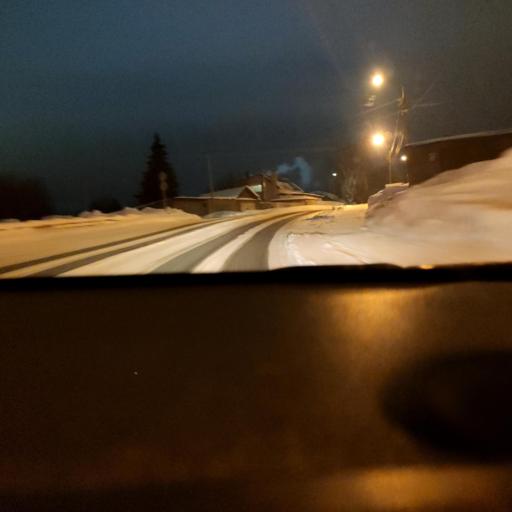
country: RU
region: Tatarstan
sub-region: Chistopol'skiy Rayon
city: Chistopol'
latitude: 55.3601
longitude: 50.6113
